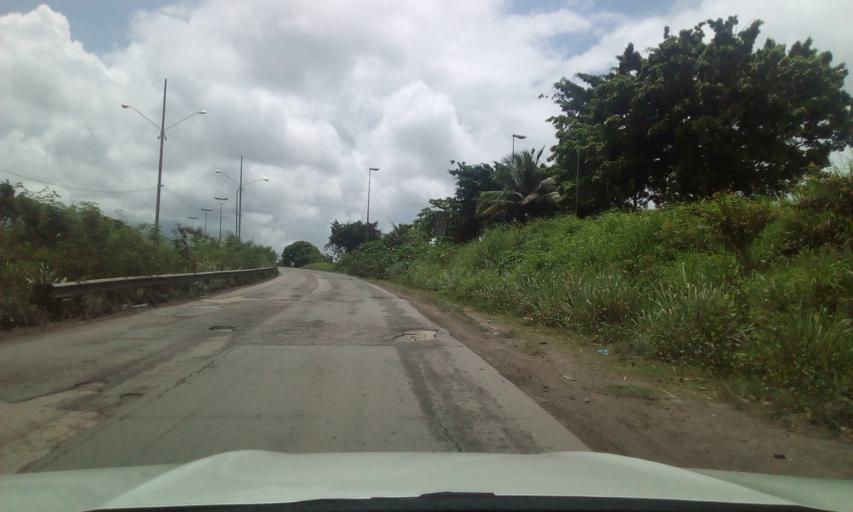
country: BR
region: Pernambuco
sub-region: Jaboatao Dos Guararapes
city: Jaboatao dos Guararapes
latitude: -8.0922
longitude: -34.9470
